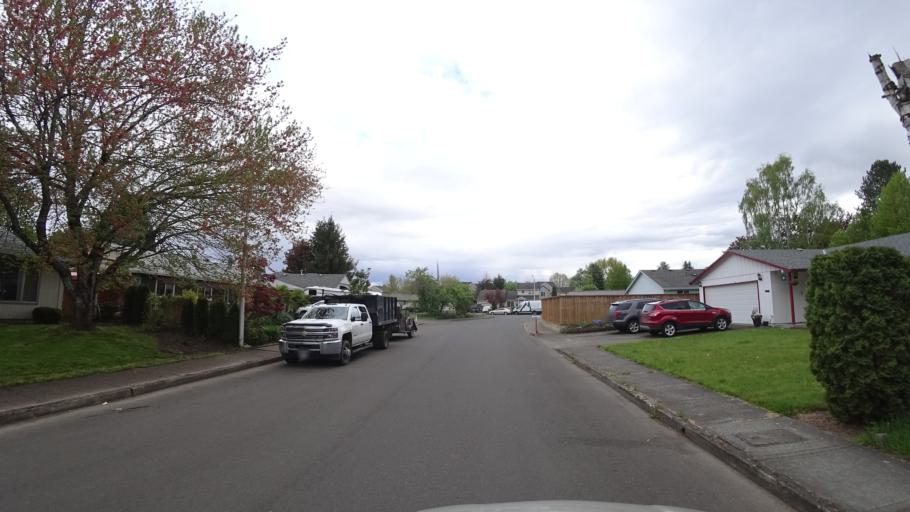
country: US
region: Oregon
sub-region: Washington County
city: Hillsboro
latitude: 45.5394
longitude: -122.9683
